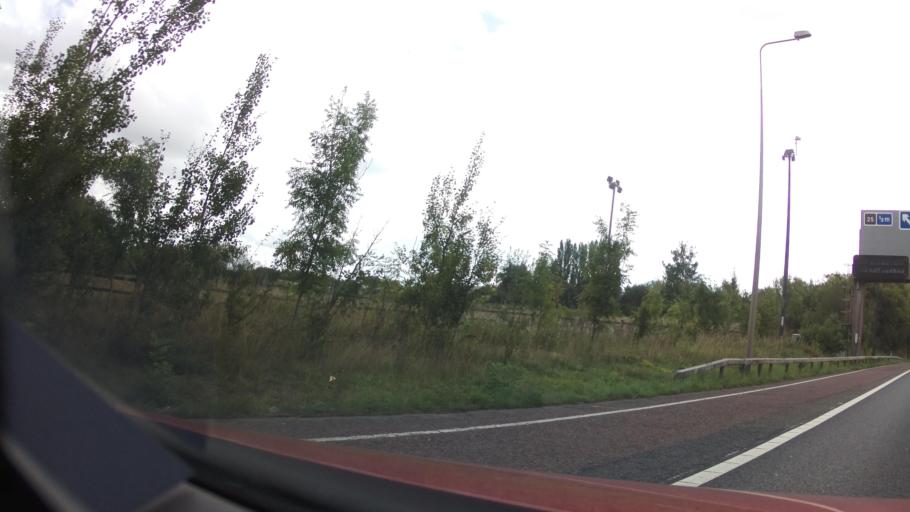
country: GB
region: England
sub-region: Borough of Tameside
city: Denton
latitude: 53.4367
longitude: -2.1289
